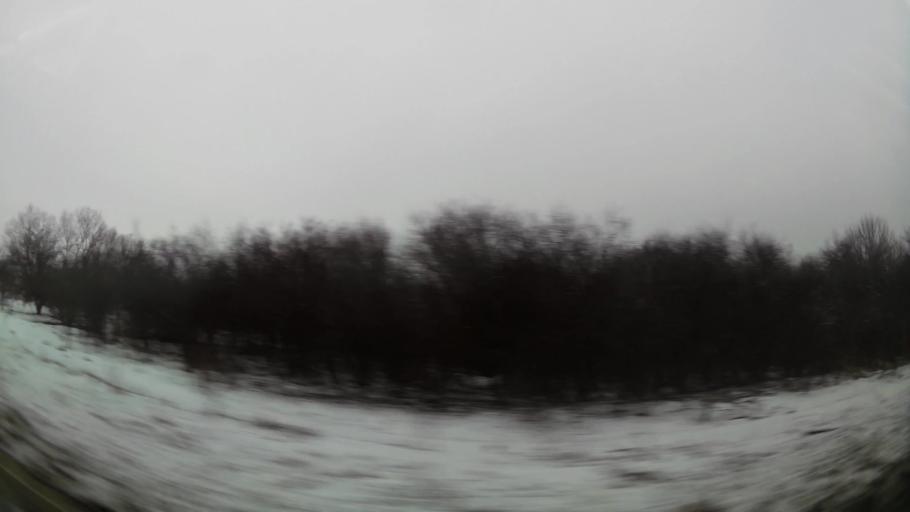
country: RS
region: Central Serbia
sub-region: Belgrade
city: Cukarica
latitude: 44.7540
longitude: 20.3808
